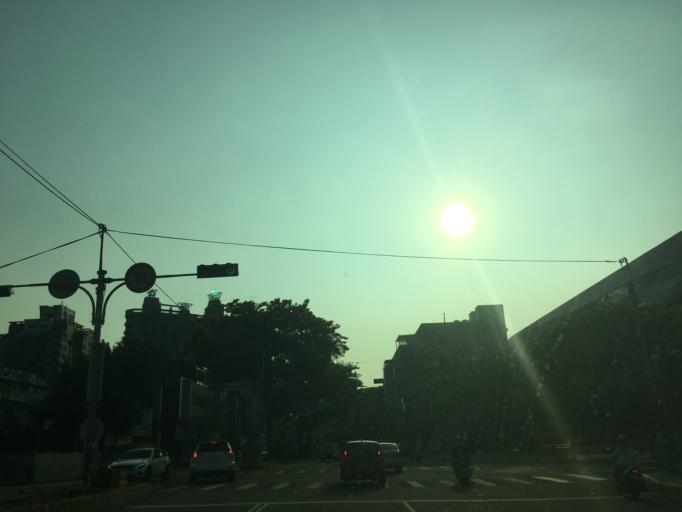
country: TW
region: Taiwan
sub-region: Taichung City
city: Taichung
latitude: 24.1265
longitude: 120.6720
